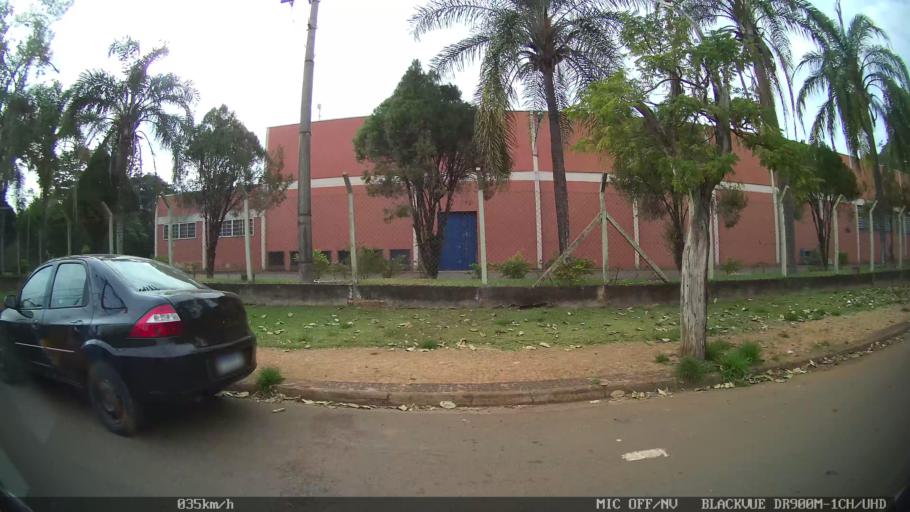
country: BR
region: Sao Paulo
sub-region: Santa Barbara D'Oeste
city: Santa Barbara d'Oeste
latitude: -22.7615
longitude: -47.3926
